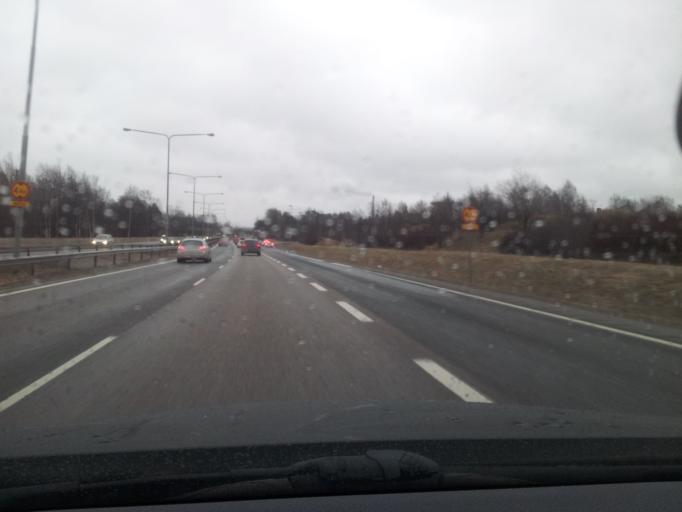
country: FI
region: Uusimaa
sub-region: Helsinki
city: Teekkarikylae
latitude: 60.1625
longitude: 24.8699
